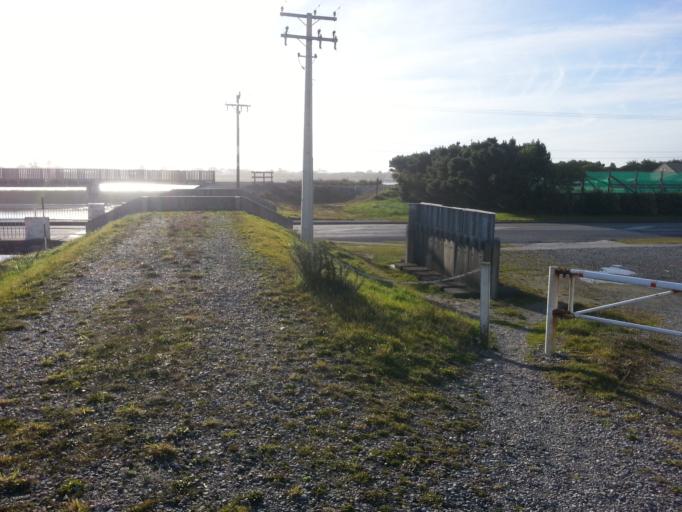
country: NZ
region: West Coast
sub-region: Grey District
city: Greymouth
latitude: -42.4525
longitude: 171.1989
